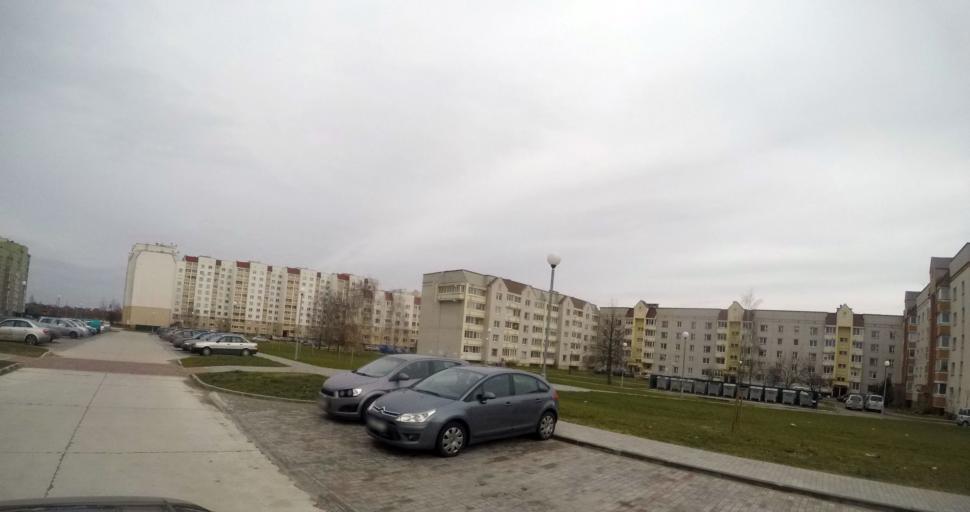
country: BY
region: Grodnenskaya
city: Hrodna
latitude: 53.7129
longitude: 23.8559
